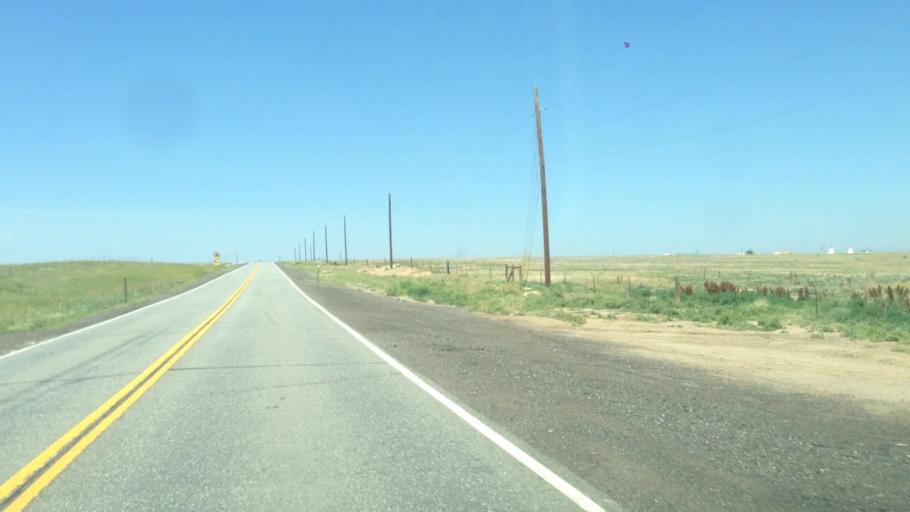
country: US
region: Colorado
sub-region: Arapahoe County
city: Dove Valley
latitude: 39.6530
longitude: -104.7280
